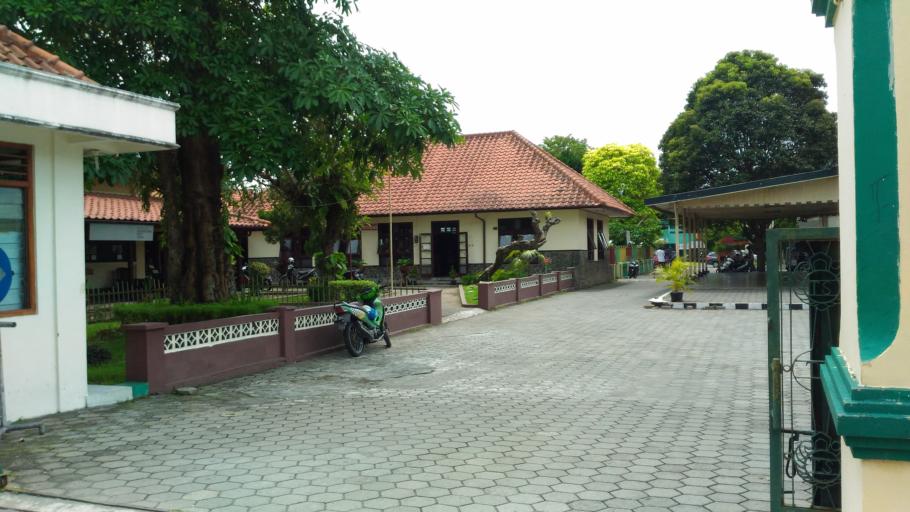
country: ID
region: Daerah Istimewa Yogyakarta
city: Yogyakarta
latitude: -7.8052
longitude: 110.3780
